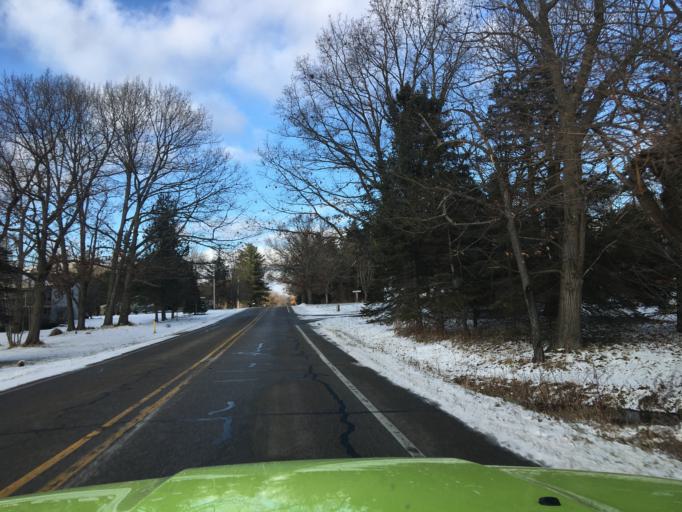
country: US
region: Michigan
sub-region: Montcalm County
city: Greenville
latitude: 43.1990
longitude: -85.2827
